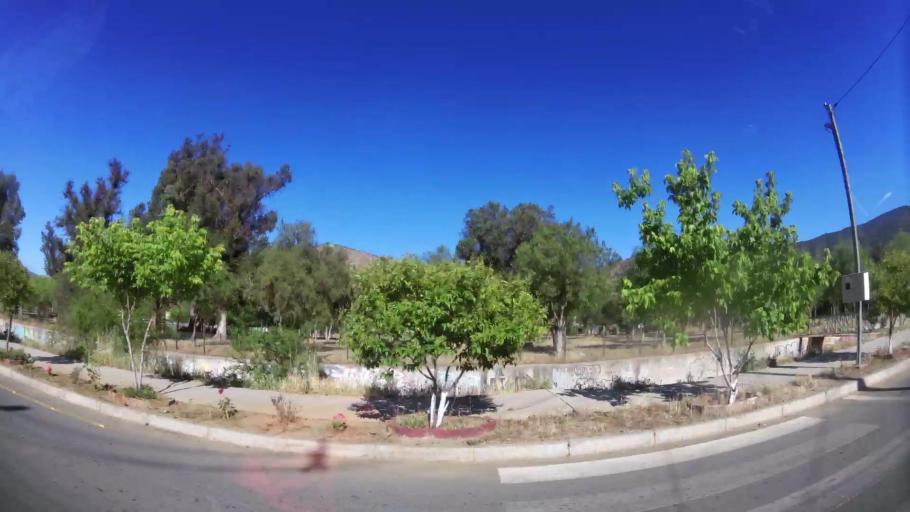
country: CL
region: Santiago Metropolitan
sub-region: Provincia de Chacabuco
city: Lampa
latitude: -33.3926
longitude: -71.1208
